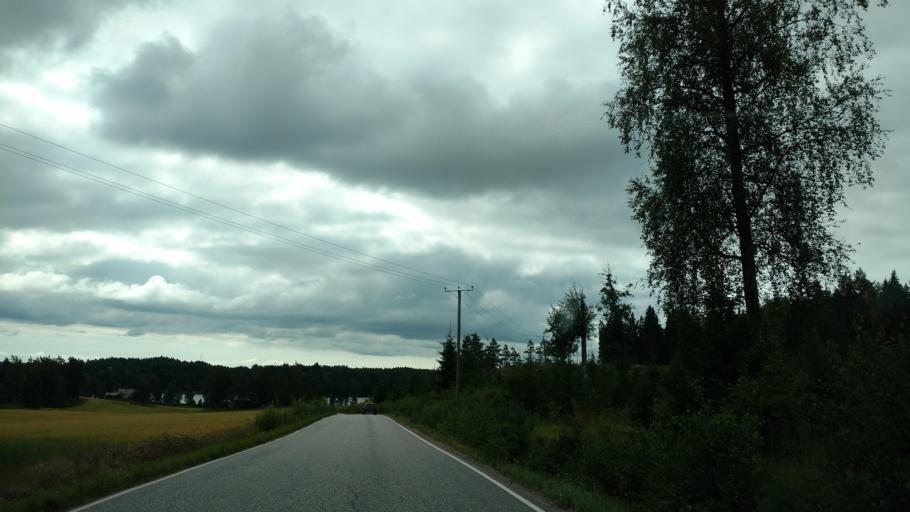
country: FI
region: Varsinais-Suomi
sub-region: Aboland-Turunmaa
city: Dragsfjaerd
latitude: 60.0592
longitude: 22.4514
